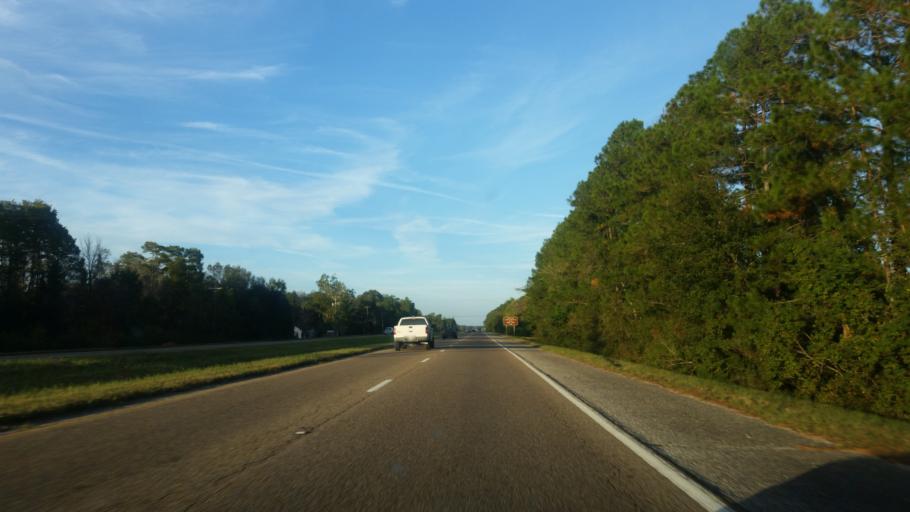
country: US
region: Mississippi
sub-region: Jackson County
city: Helena
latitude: 30.4418
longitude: -88.4322
